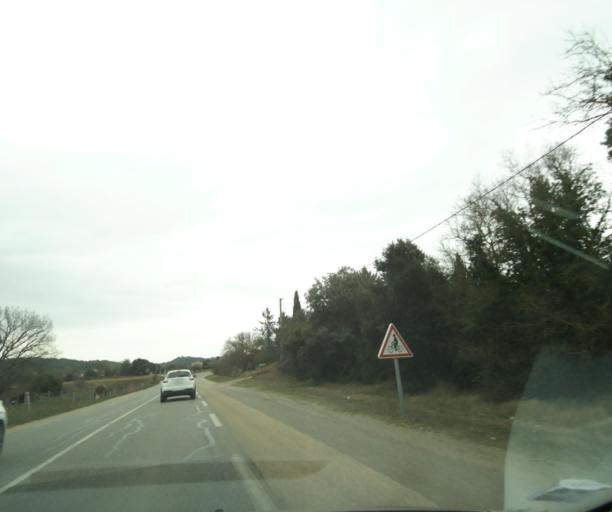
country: FR
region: Provence-Alpes-Cote d'Azur
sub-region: Departement des Bouches-du-Rhone
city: Peyrolles-en-Provence
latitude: 43.6416
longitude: 5.6117
